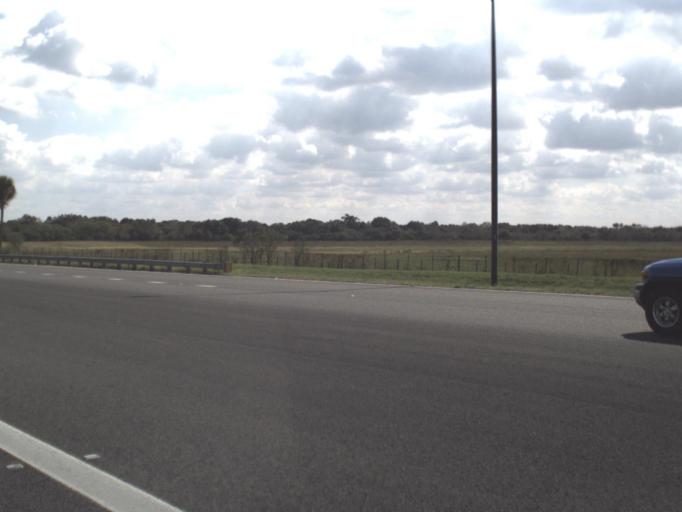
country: US
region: Florida
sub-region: Polk County
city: Lakeland Highlands
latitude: 27.9956
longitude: -81.9337
